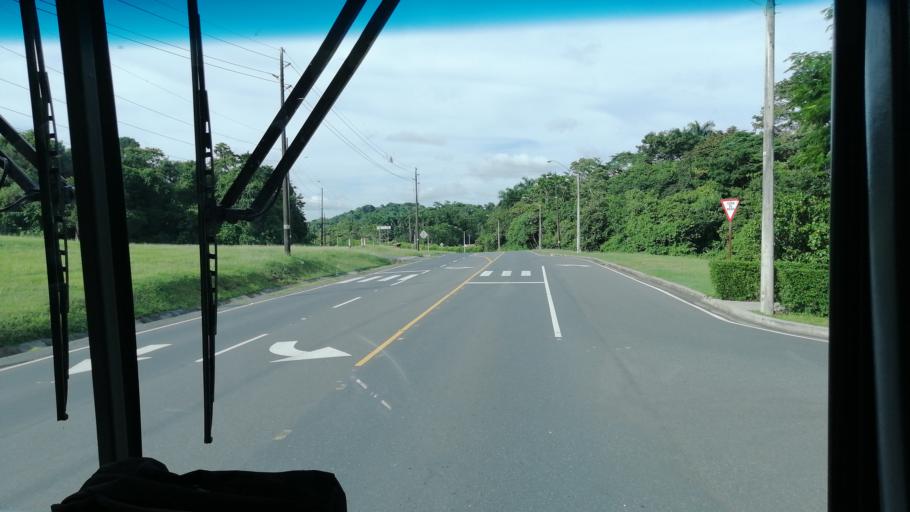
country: PA
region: Panama
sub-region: Distrito de Panama
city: Ancon
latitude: 8.9307
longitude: -79.5918
